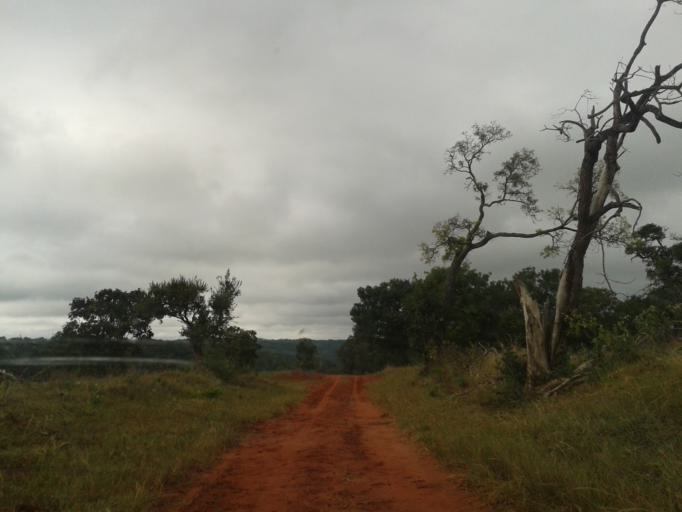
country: BR
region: Minas Gerais
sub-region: Campina Verde
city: Campina Verde
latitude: -19.4189
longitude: -49.6318
